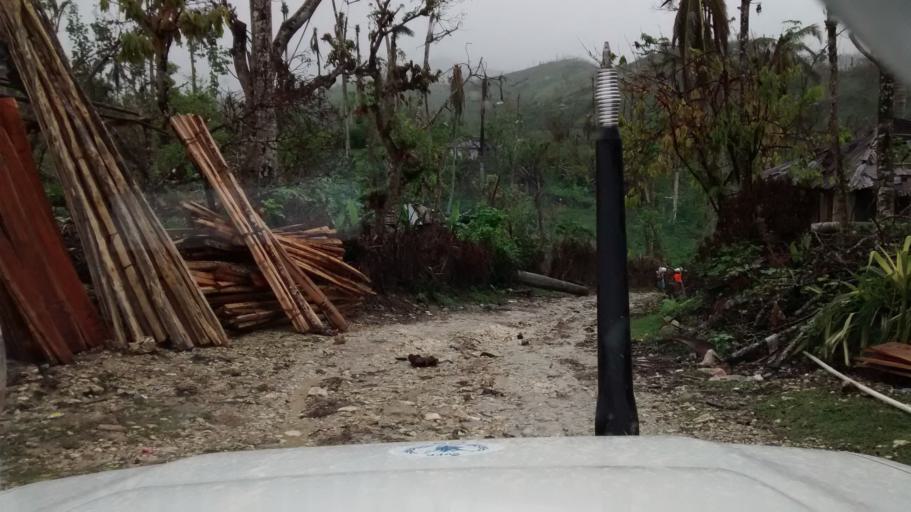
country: HT
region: Grandans
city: Moron
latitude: 18.5356
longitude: -74.1557
